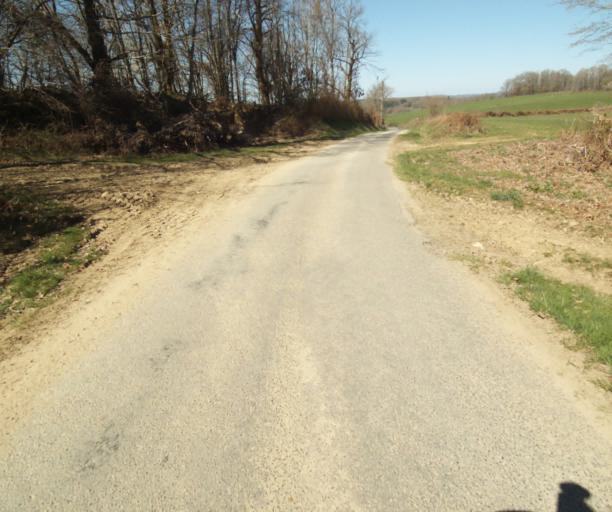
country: FR
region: Limousin
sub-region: Departement de la Correze
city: Chamboulive
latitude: 45.4432
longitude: 1.6812
